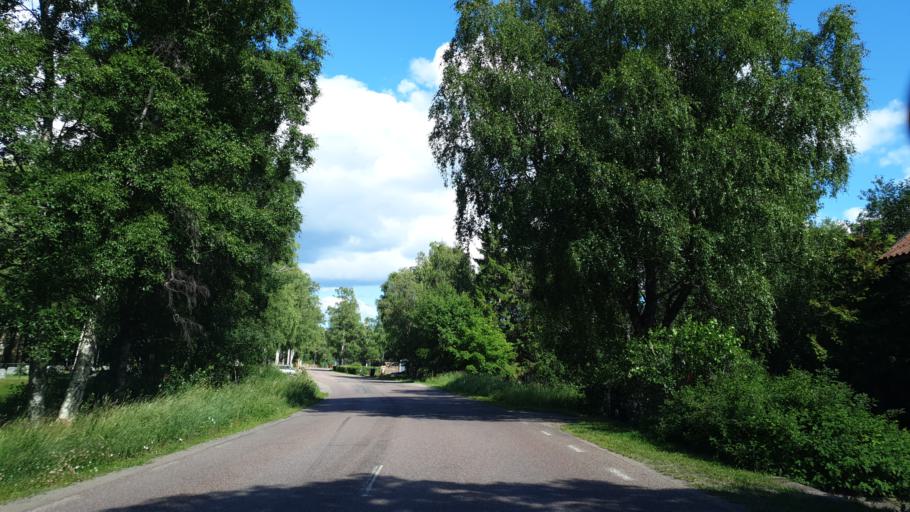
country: SE
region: Gaevleborg
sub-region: Nordanstigs Kommun
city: Bergsjoe
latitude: 62.0470
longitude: 17.2444
